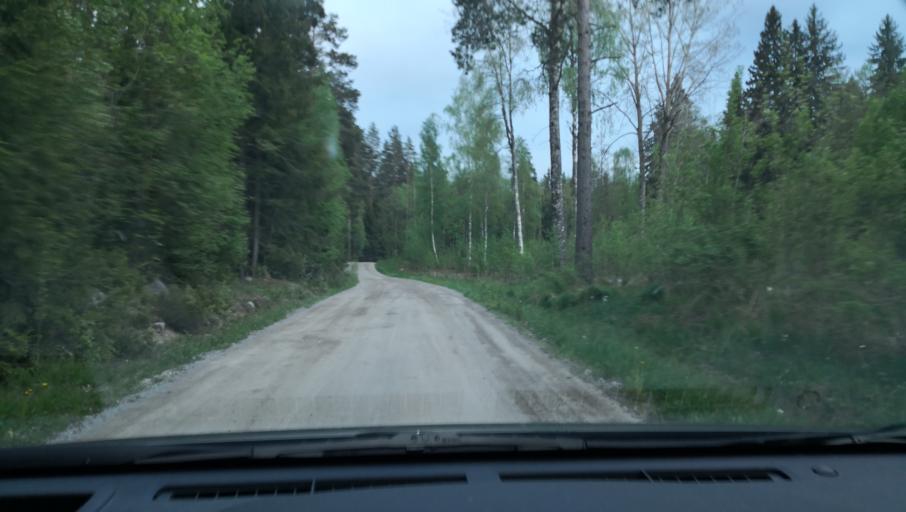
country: SE
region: Vaestmanland
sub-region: Skinnskattebergs Kommun
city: Skinnskatteberg
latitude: 59.7317
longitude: 15.4744
